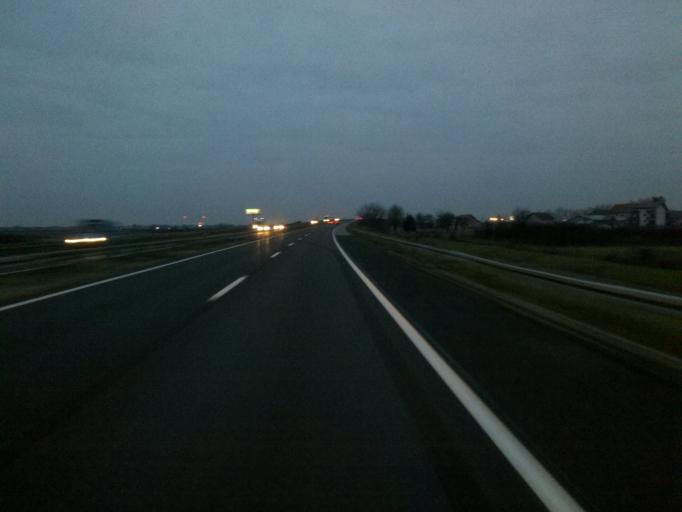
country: HR
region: Zagrebacka
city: Micevec
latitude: 45.7465
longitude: 16.0515
